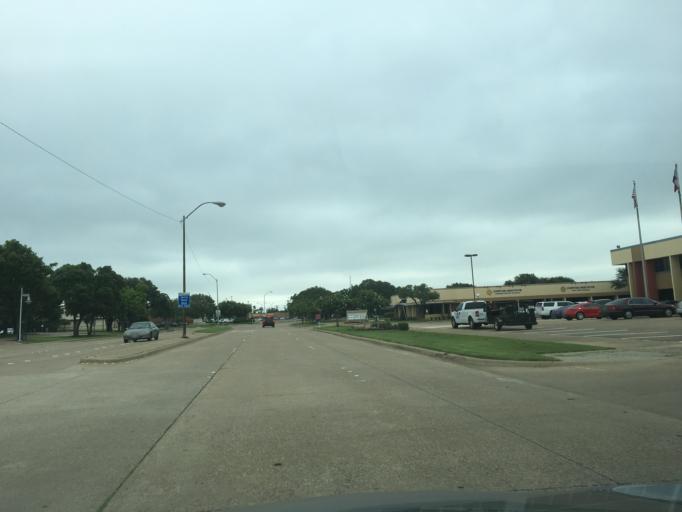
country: US
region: Texas
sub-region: Dallas County
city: Richardson
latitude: 32.9375
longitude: -96.7415
